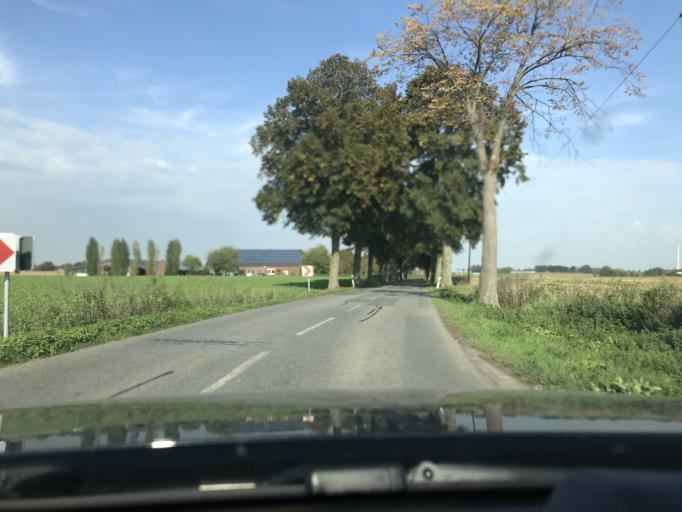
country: DE
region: North Rhine-Westphalia
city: Kalkar
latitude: 51.7017
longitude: 6.2642
